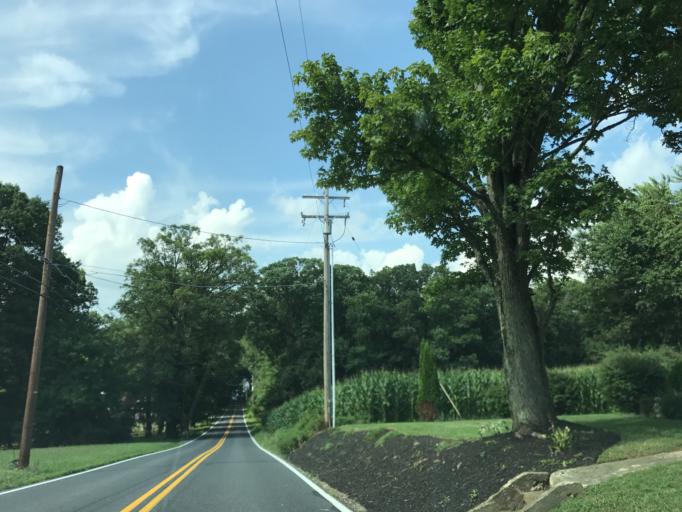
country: US
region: Pennsylvania
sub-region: York County
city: Pennville
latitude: 39.7434
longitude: -77.0006
